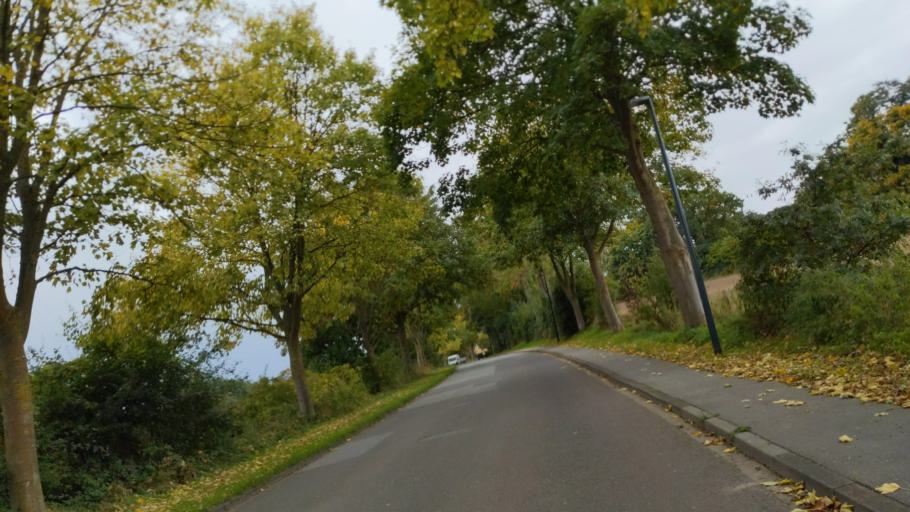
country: DE
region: Schleswig-Holstein
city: Scharbeutz
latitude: 54.0457
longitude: 10.7362
